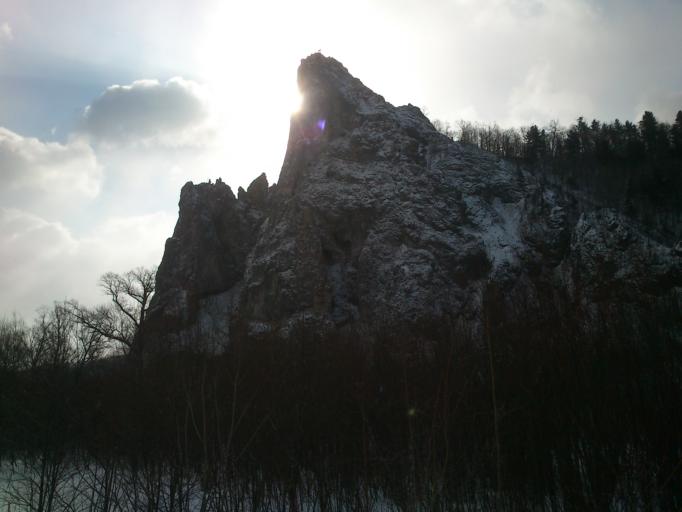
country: RU
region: Primorskiy
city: Kavalerovo
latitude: 44.2488
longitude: 135.0591
